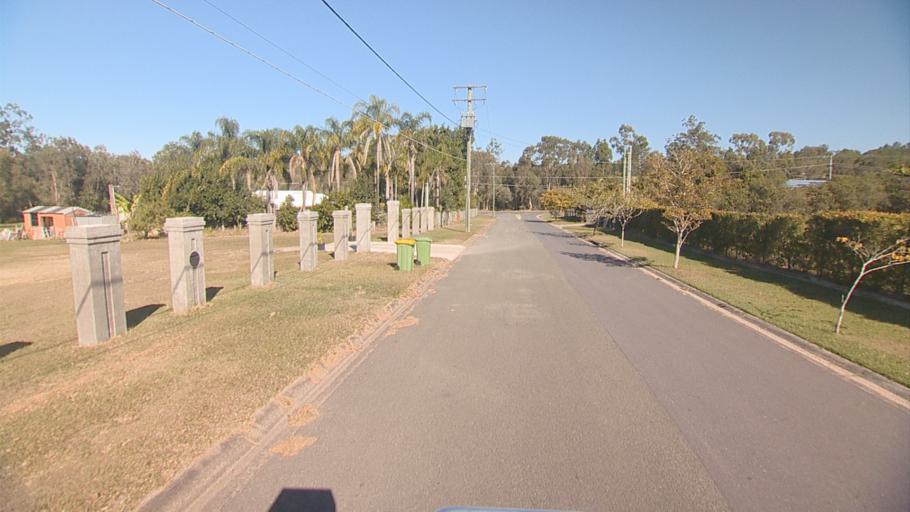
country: AU
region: Queensland
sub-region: Logan
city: Logan Reserve
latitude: -27.7046
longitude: 153.0705
